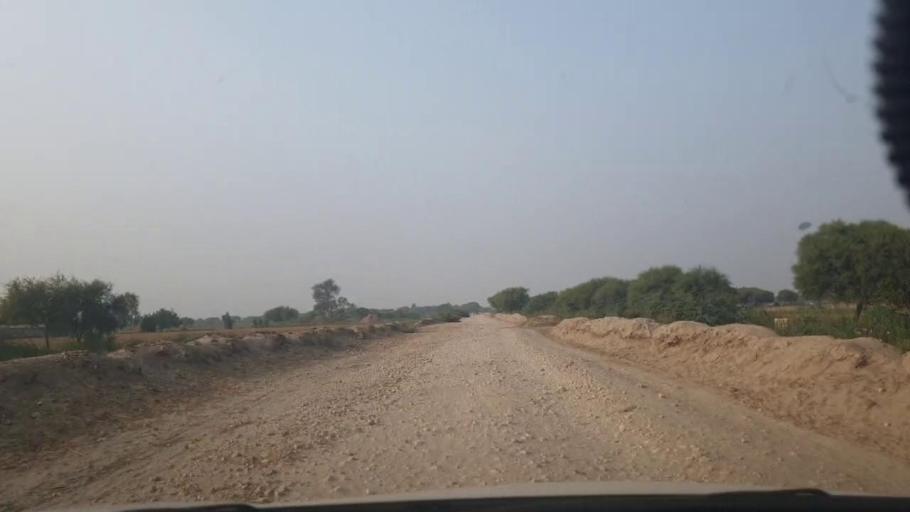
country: PK
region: Sindh
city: Bulri
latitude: 24.7984
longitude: 68.4149
